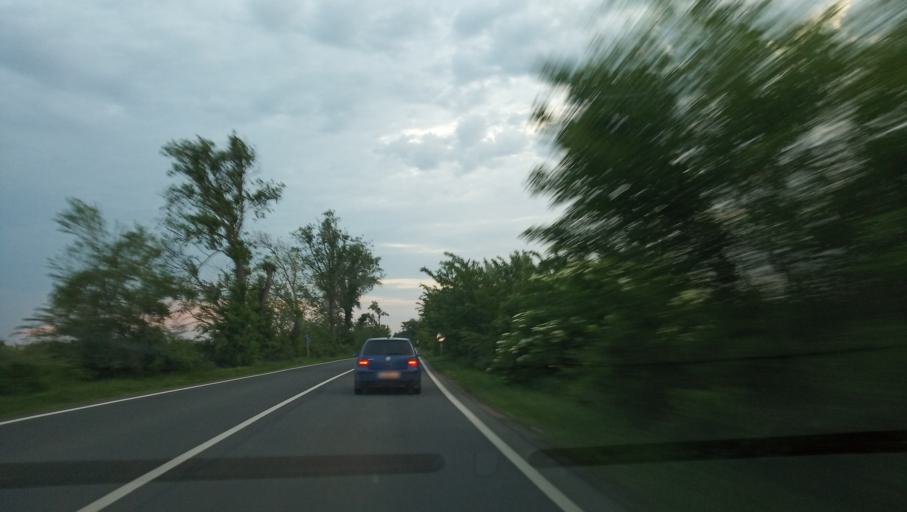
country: RO
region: Timis
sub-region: Comuna Sag
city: Sag
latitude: 45.6209
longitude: 21.1924
